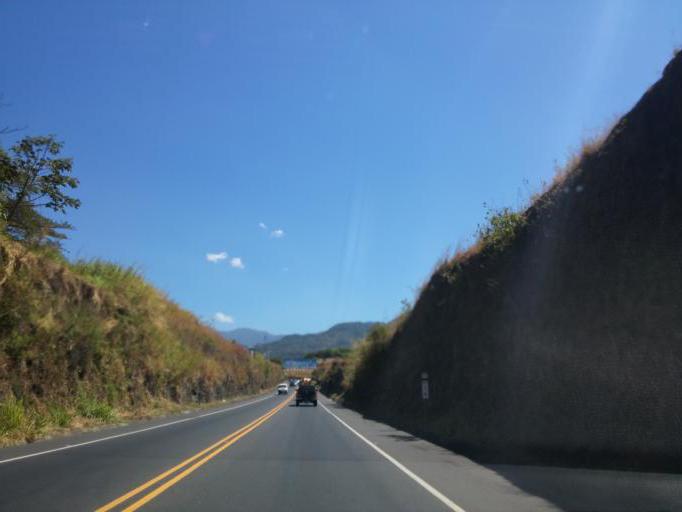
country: CR
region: Heredia
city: Colon
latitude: 9.9458
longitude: -84.2310
